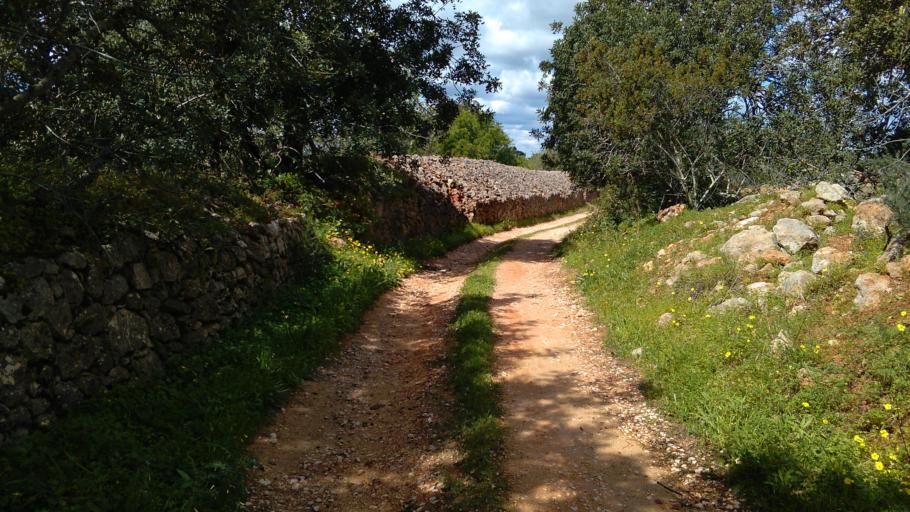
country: PT
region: Faro
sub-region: Albufeira
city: Albufeira
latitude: 37.0964
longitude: -8.2769
